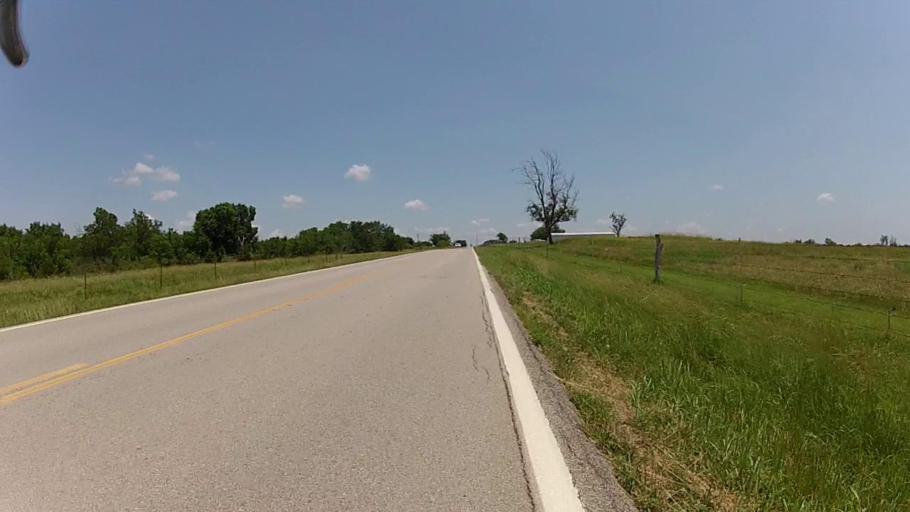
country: US
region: Kansas
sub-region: Montgomery County
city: Cherryvale
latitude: 37.1929
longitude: -95.4843
